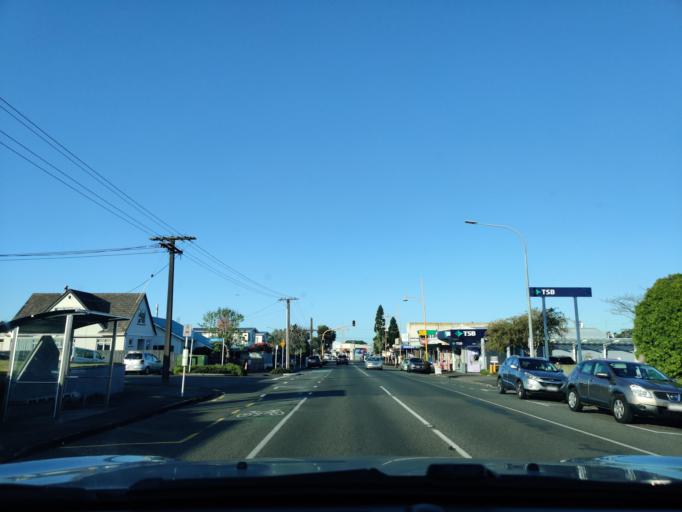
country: NZ
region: Taranaki
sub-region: New Plymouth District
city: New Plymouth
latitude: -39.0720
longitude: 174.0613
